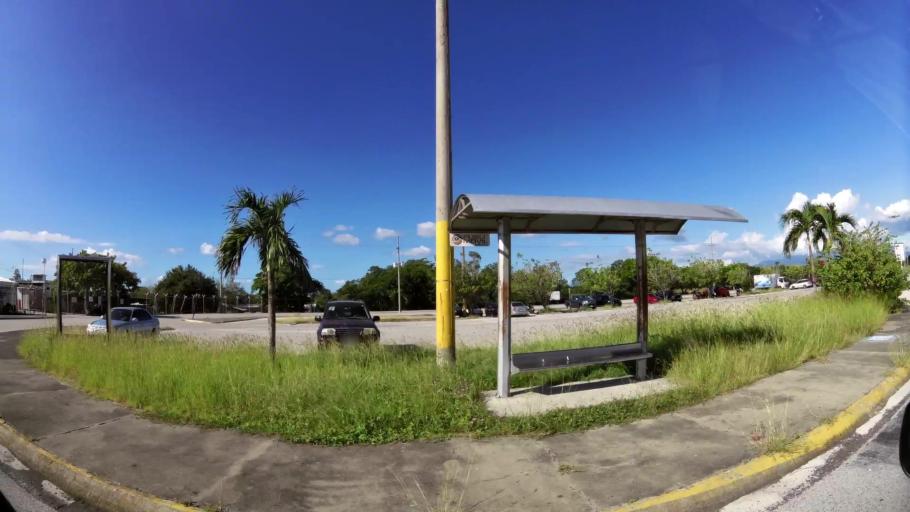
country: CR
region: Guanacaste
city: Liberia
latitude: 10.5998
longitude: -85.5389
